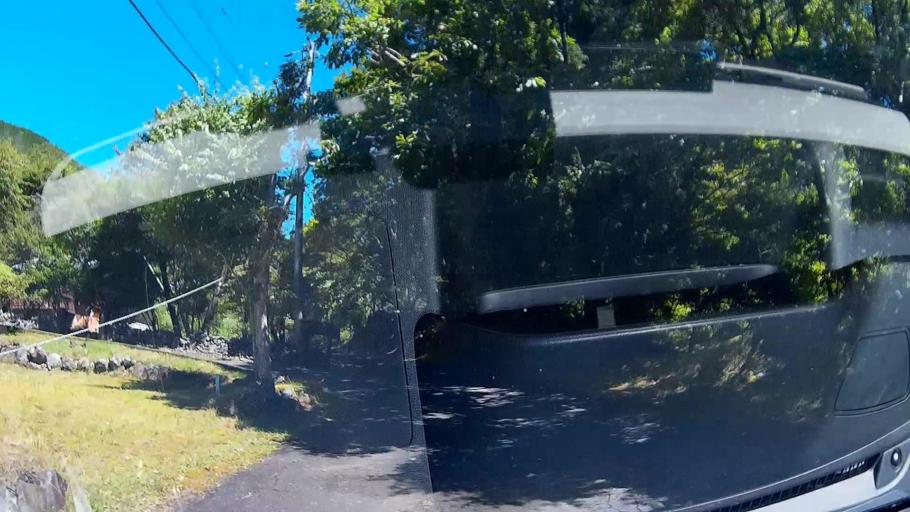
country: JP
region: Shizuoka
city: Fujinomiya
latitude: 35.2846
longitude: 138.3196
